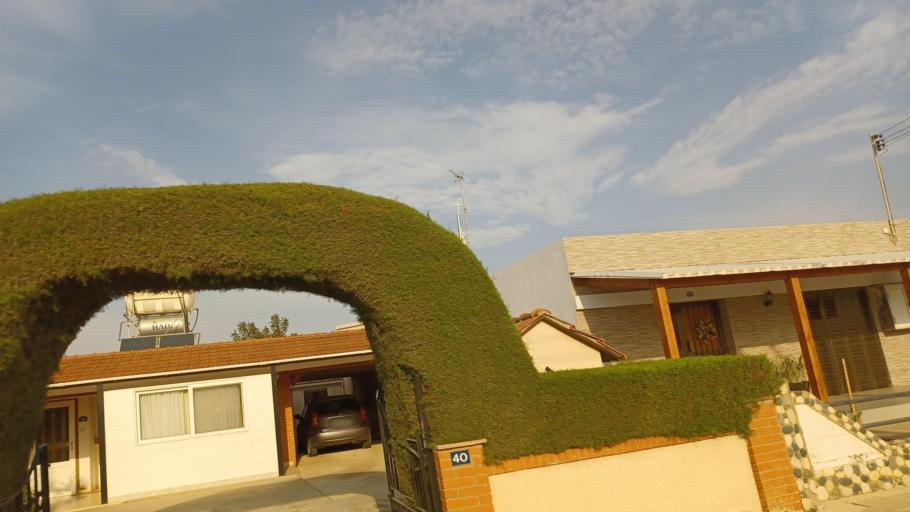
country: CY
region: Ammochostos
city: Frenaros
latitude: 35.0442
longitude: 33.9206
